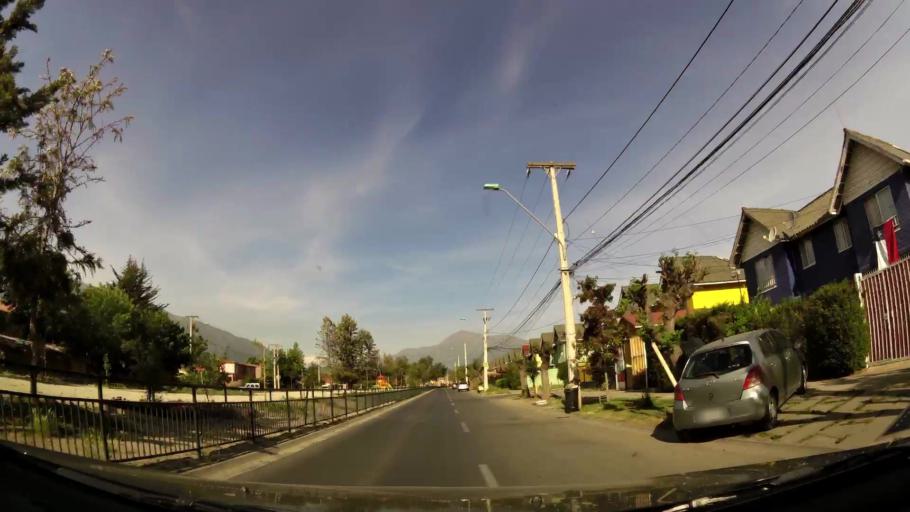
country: CL
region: Santiago Metropolitan
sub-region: Provincia de Cordillera
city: Puente Alto
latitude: -33.5872
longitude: -70.5611
